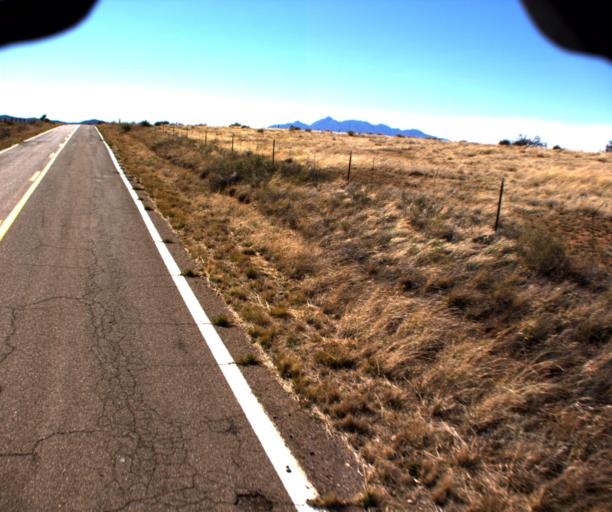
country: US
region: Arizona
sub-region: Cochise County
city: Huachuca City
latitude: 31.6008
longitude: -110.5722
